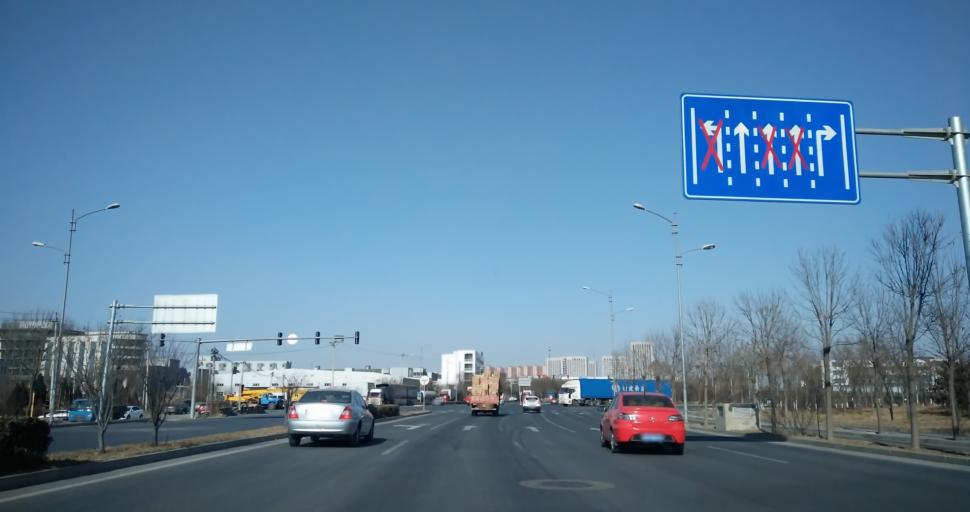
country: CN
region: Beijing
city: Qingyundian
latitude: 39.7375
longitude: 116.4954
